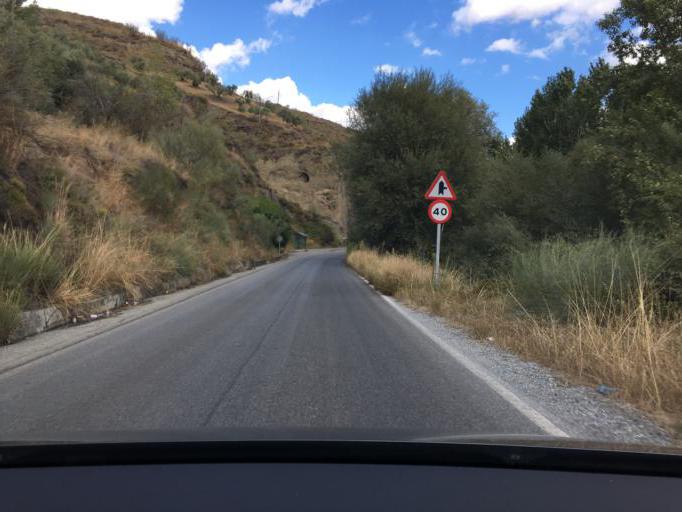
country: ES
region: Andalusia
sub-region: Provincia de Granada
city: Dudar
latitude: 37.1826
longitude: -3.4933
